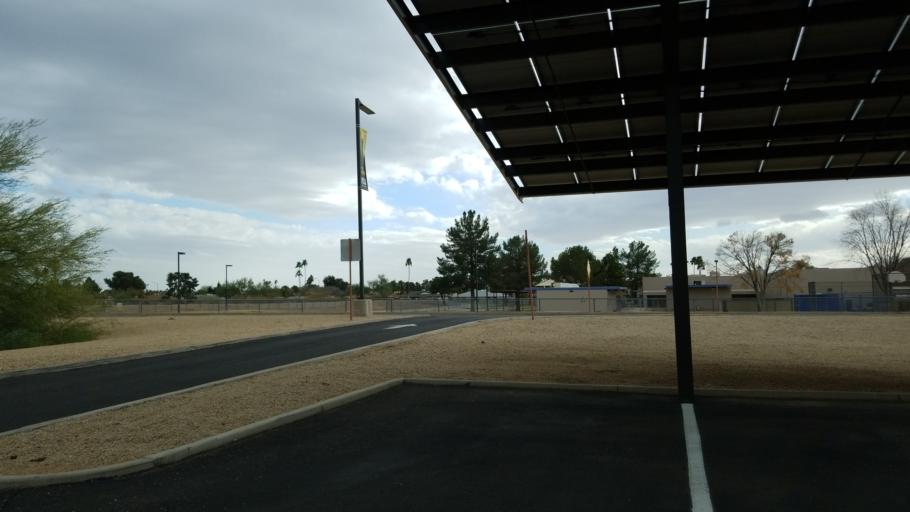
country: US
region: Arizona
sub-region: Maricopa County
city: Glendale
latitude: 33.6056
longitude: -112.1562
